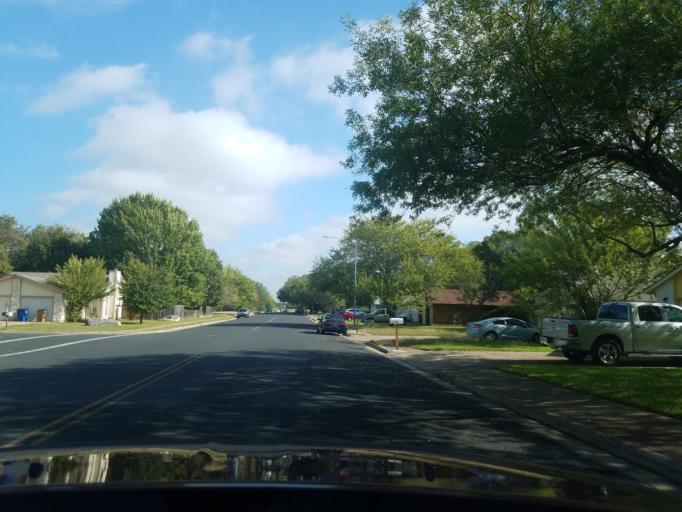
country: US
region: Texas
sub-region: Williamson County
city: Jollyville
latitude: 30.4476
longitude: -97.7756
